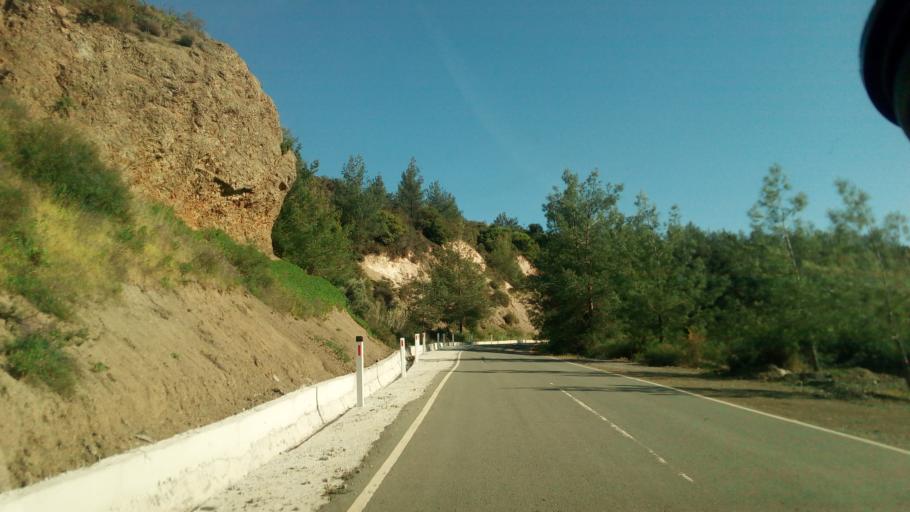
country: CY
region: Limassol
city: Pachna
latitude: 34.8818
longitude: 32.7519
